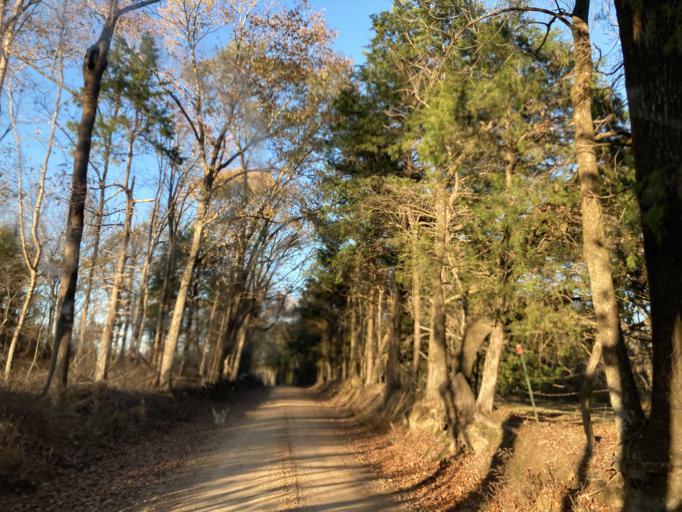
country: US
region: Mississippi
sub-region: Yazoo County
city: Yazoo City
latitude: 32.9437
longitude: -90.2860
